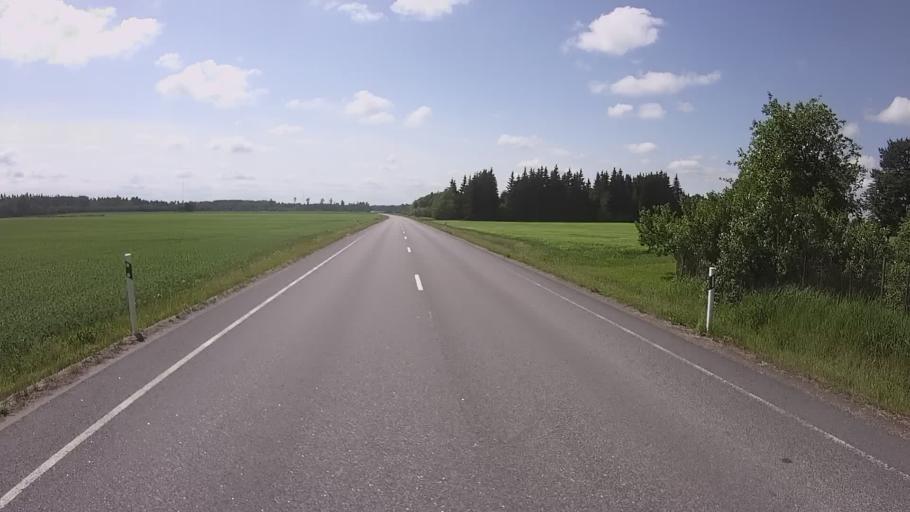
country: EE
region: Tartu
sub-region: Tartu linn
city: Tartu
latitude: 58.3932
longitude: 26.8929
